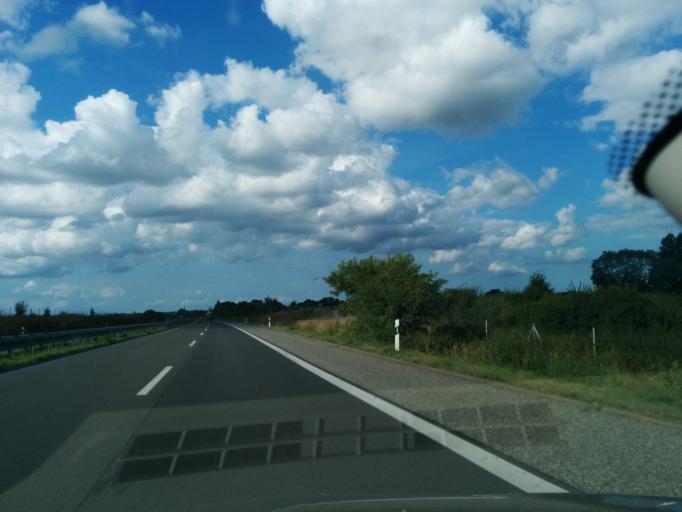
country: DE
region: Brandenburg
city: Schonfeld
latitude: 53.4278
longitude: 13.9969
